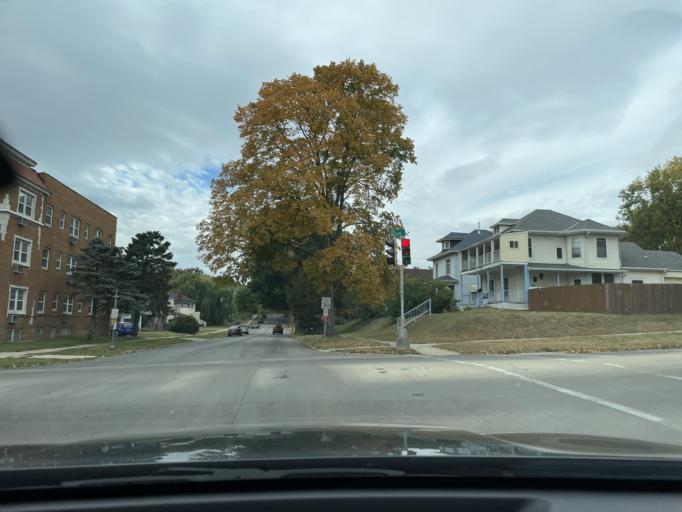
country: US
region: Missouri
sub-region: Buchanan County
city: Saint Joseph
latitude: 39.7692
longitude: -94.8246
